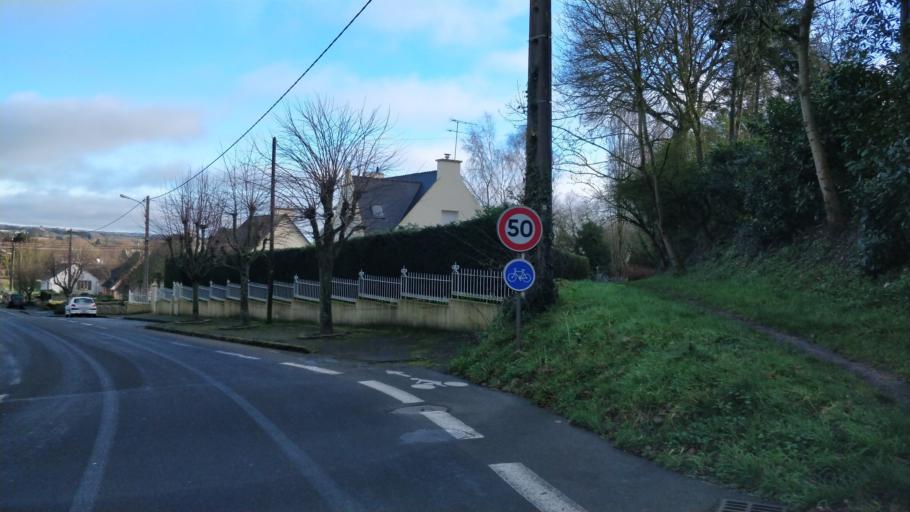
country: FR
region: Brittany
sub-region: Departement des Cotes-d'Armor
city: Lamballe
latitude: 48.4636
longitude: -2.5298
